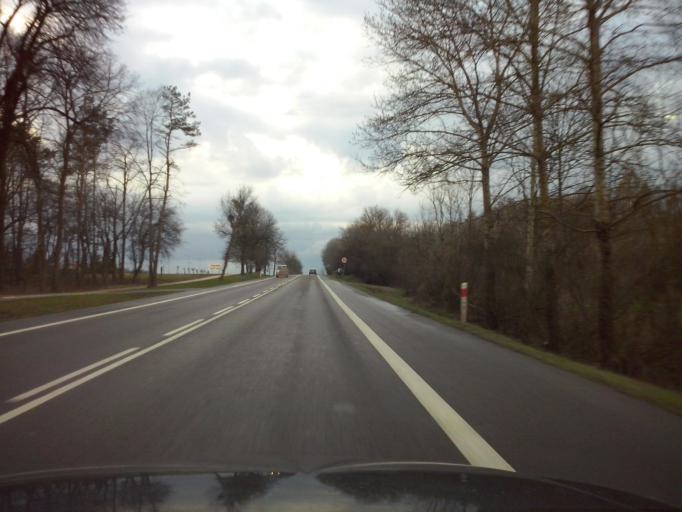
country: PL
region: Lublin Voivodeship
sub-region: Chelm
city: Chelm
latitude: 51.1577
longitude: 23.4027
